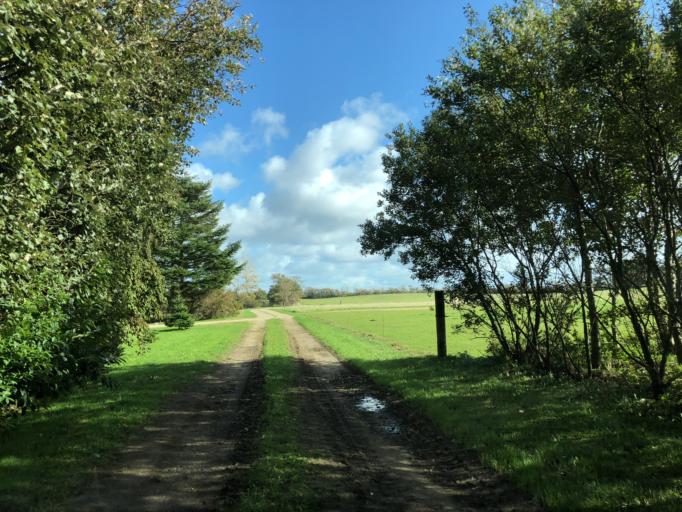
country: DK
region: Central Jutland
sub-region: Holstebro Kommune
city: Ulfborg
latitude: 56.2938
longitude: 8.3200
